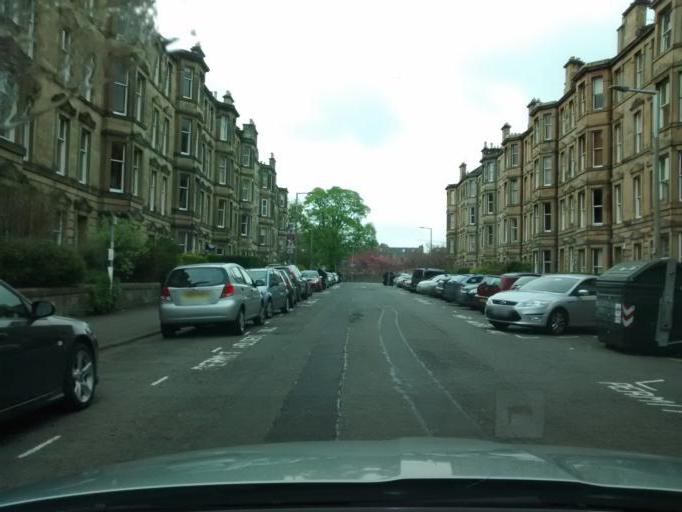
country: GB
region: Scotland
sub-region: Edinburgh
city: Edinburgh
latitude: 55.9272
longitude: -3.2041
